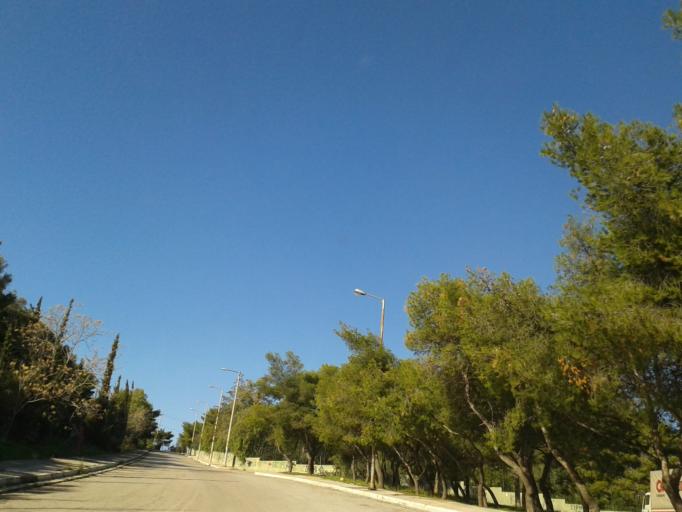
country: GR
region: Attica
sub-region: Nomarchia Athinas
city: Galatsi
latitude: 38.0049
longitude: 23.7579
